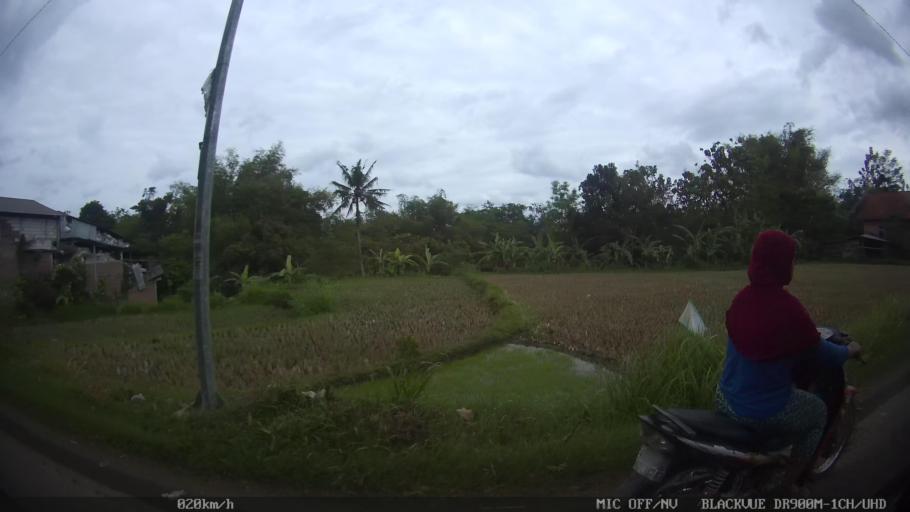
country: ID
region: Daerah Istimewa Yogyakarta
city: Sewon
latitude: -7.8601
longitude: 110.4236
